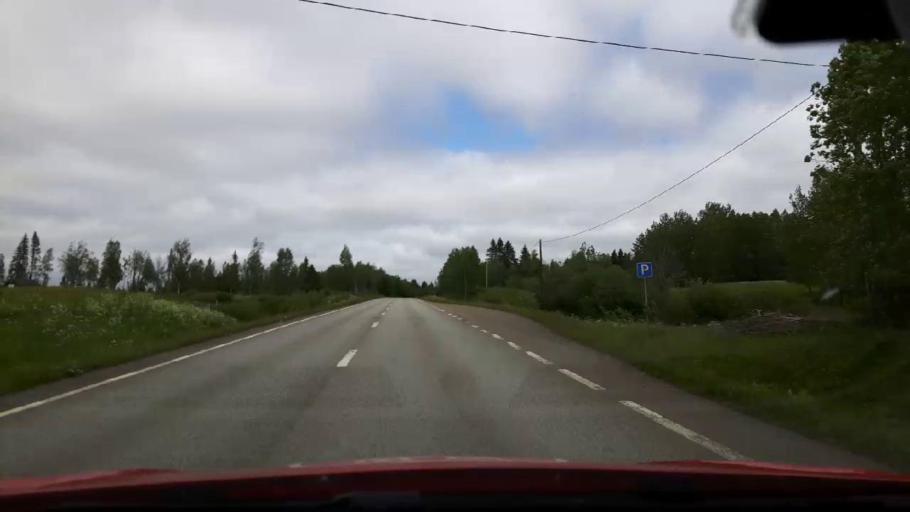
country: SE
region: Jaemtland
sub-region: Krokoms Kommun
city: Krokom
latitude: 63.5186
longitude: 14.5331
